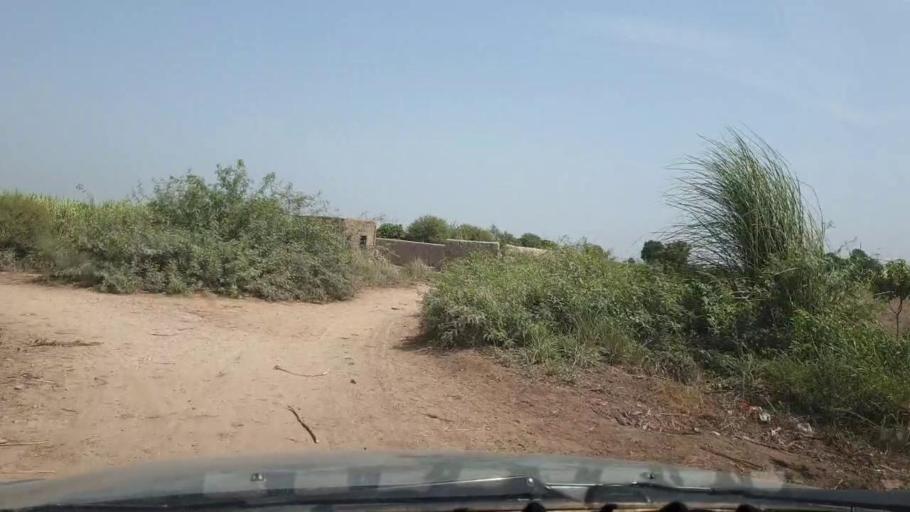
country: PK
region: Sindh
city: Tando Muhammad Khan
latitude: 25.1812
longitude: 68.6331
